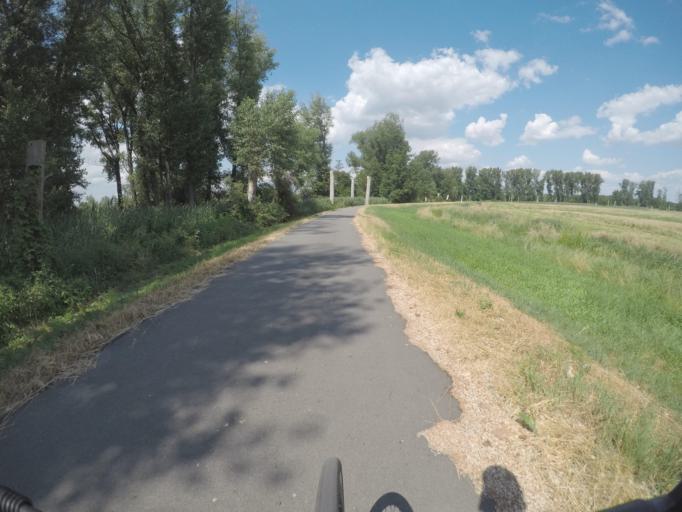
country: DE
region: Brandenburg
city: Roskow
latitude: 52.4366
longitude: 12.6616
